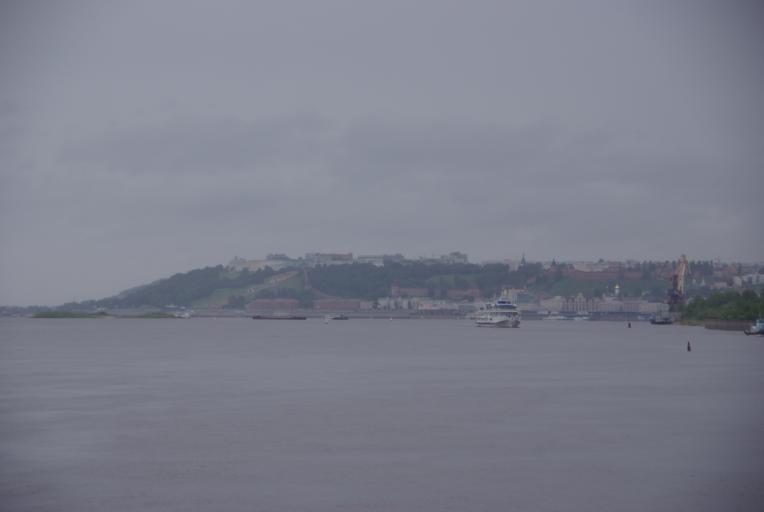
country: RU
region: Nizjnij Novgorod
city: Nizhniy Novgorod
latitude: 56.3381
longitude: 43.9721
